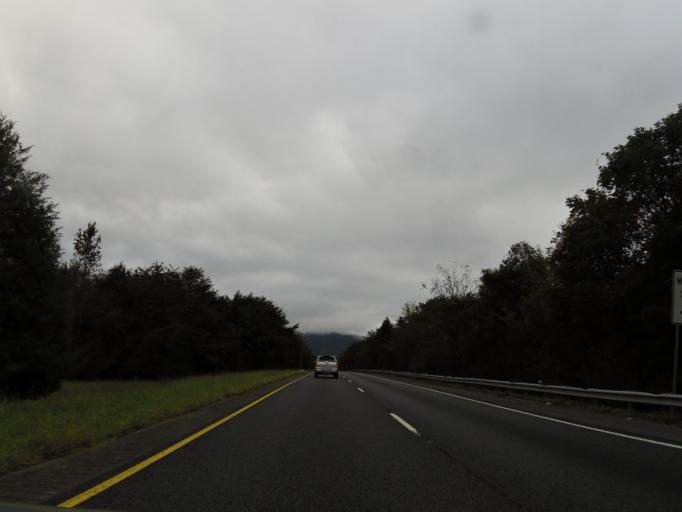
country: US
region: Georgia
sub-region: Dade County
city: Trenton
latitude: 34.9508
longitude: -85.4666
